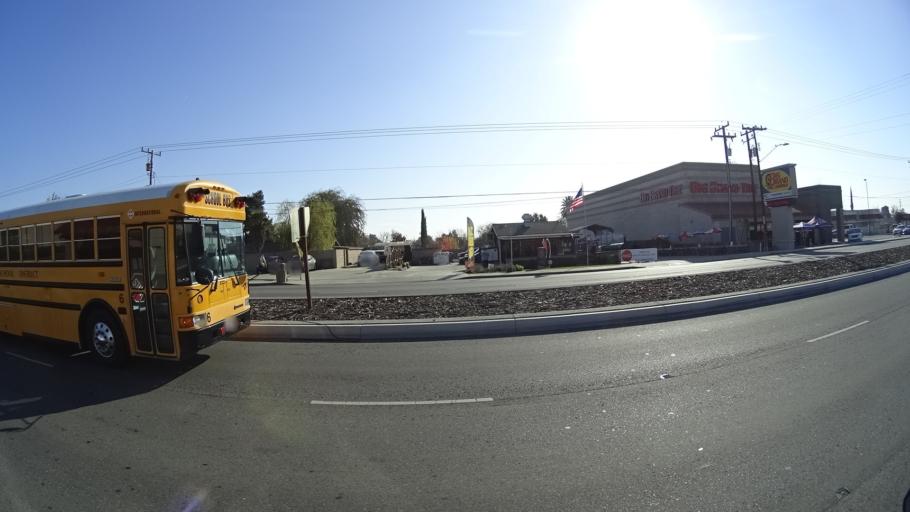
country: US
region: California
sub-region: Kern County
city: Greenacres
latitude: 35.3835
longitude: -119.1074
